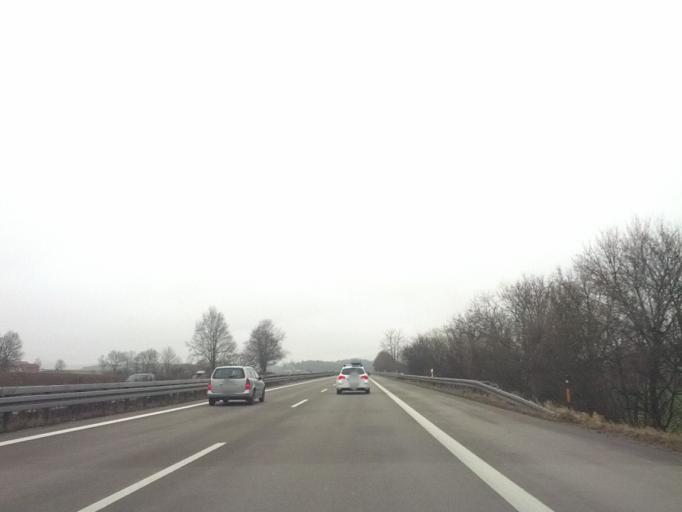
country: DE
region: Bavaria
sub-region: Swabia
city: Lauben
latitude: 47.7999
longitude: 10.3145
